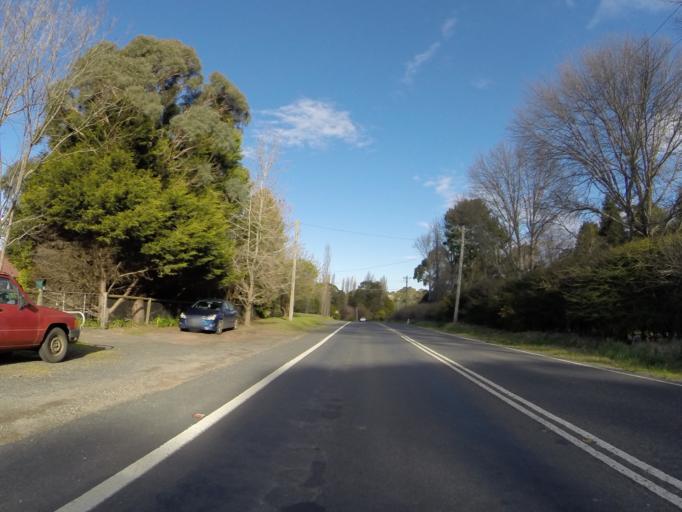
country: AU
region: New South Wales
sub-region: Wingecarribee
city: Moss Vale
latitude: -34.5509
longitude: 150.3885
